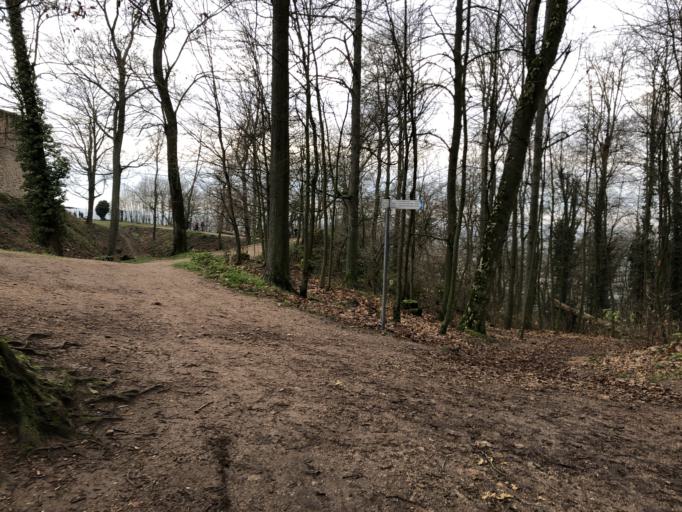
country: DE
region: Baden-Wuerttemberg
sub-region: Karlsruhe Region
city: Dossenheim
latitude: 49.4596
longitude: 8.6798
